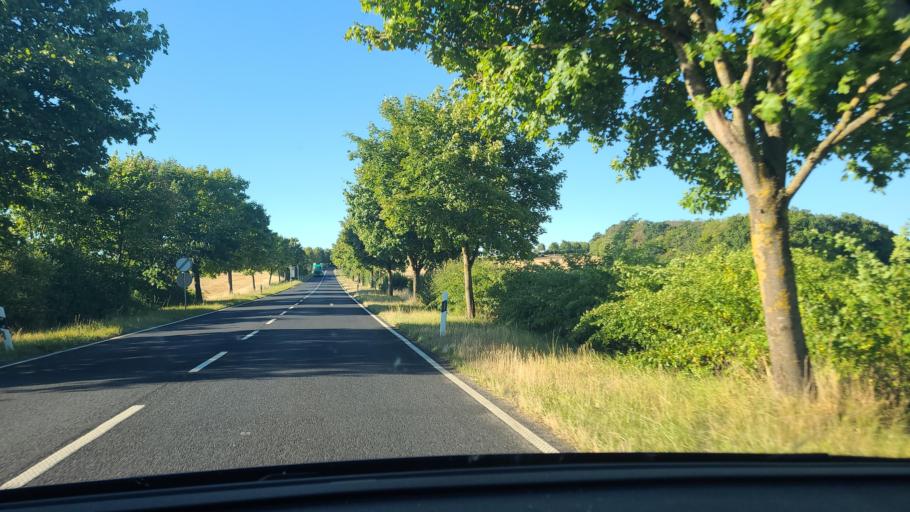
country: LU
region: Luxembourg
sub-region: Canton de Capellen
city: Garnich
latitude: 49.6326
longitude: 5.9559
